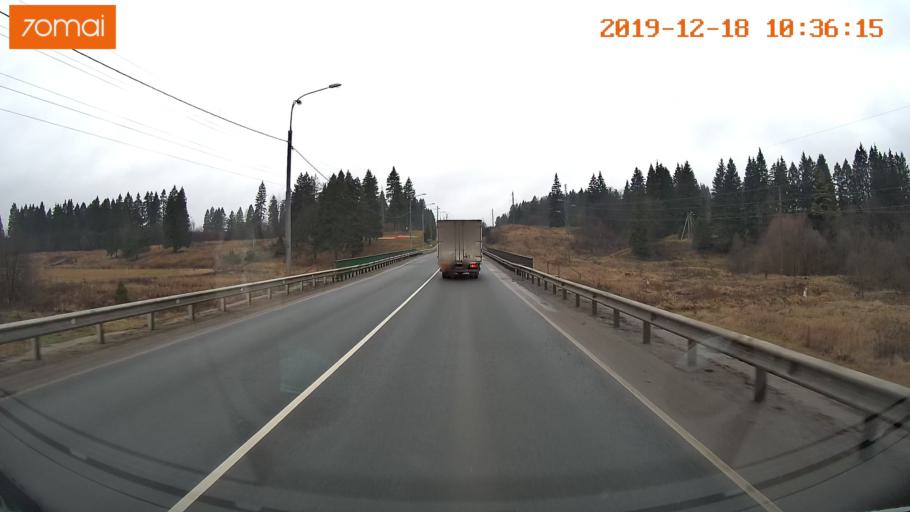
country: RU
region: Moskovskaya
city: Troitsk
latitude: 55.4191
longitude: 37.1880
